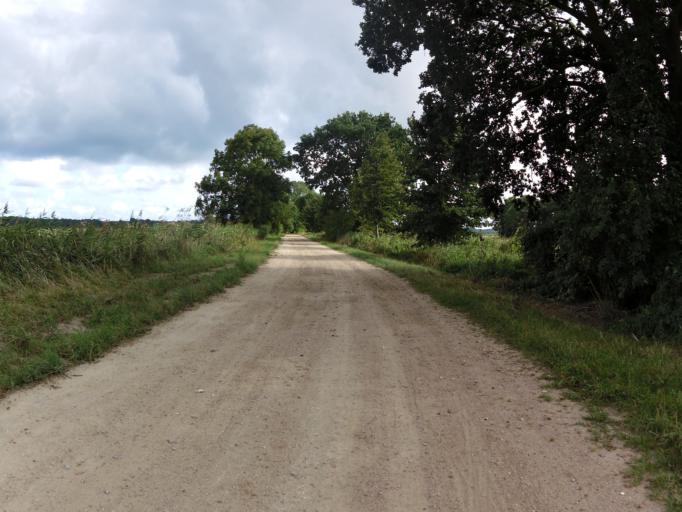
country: DE
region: Mecklenburg-Vorpommern
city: Loddin
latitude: 53.9880
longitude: 14.0572
